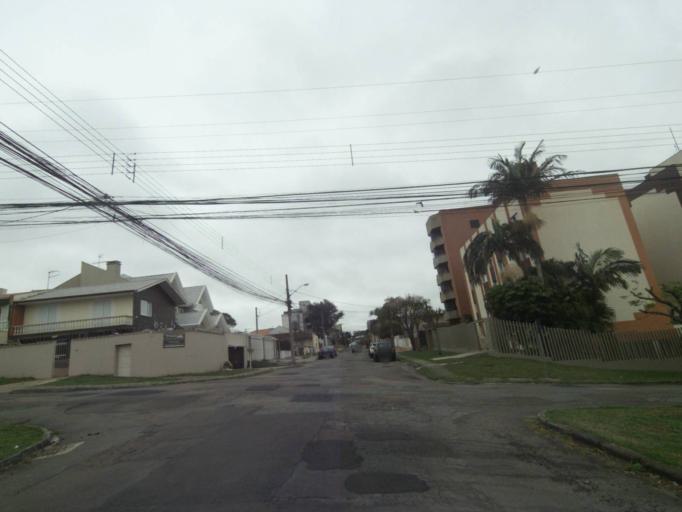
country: BR
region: Parana
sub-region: Curitiba
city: Curitiba
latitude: -25.4732
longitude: -49.2840
